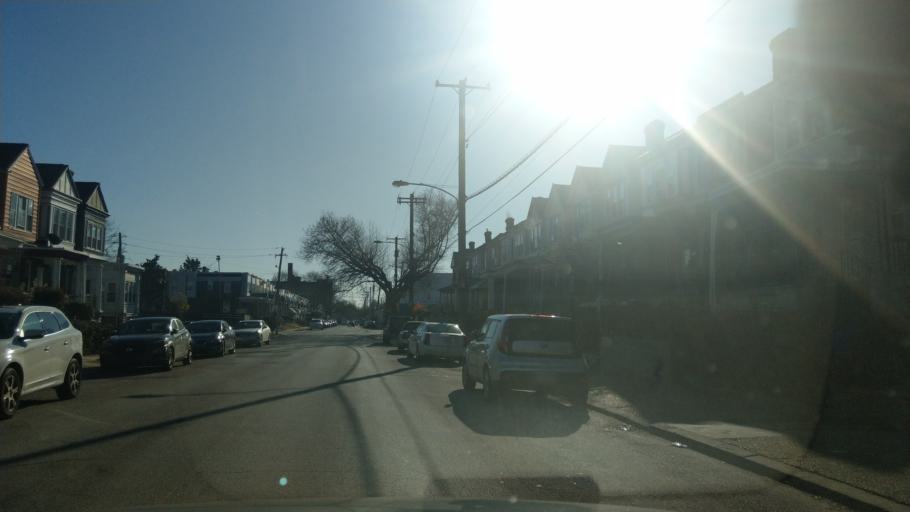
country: US
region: Pennsylvania
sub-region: Montgomery County
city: Wyncote
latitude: 40.0573
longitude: -75.1526
